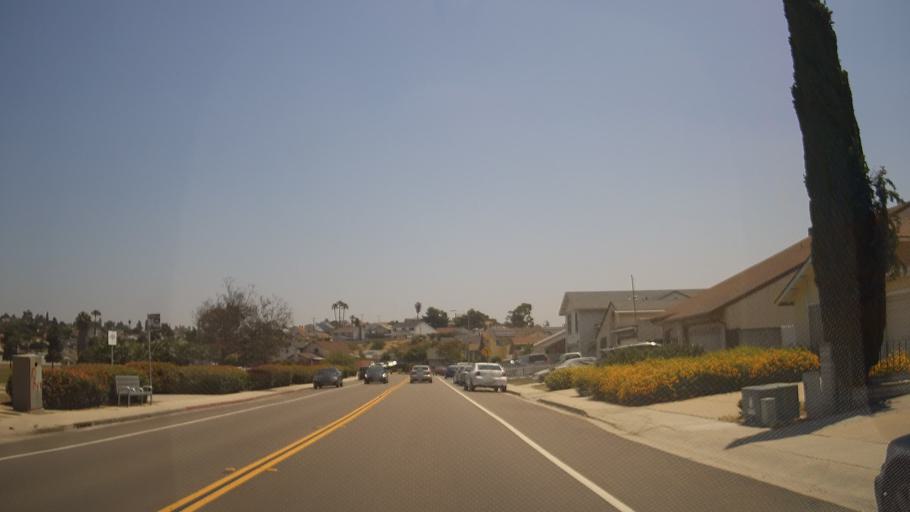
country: US
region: California
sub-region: San Diego County
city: Bonita
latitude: 32.6669
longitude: -117.0520
